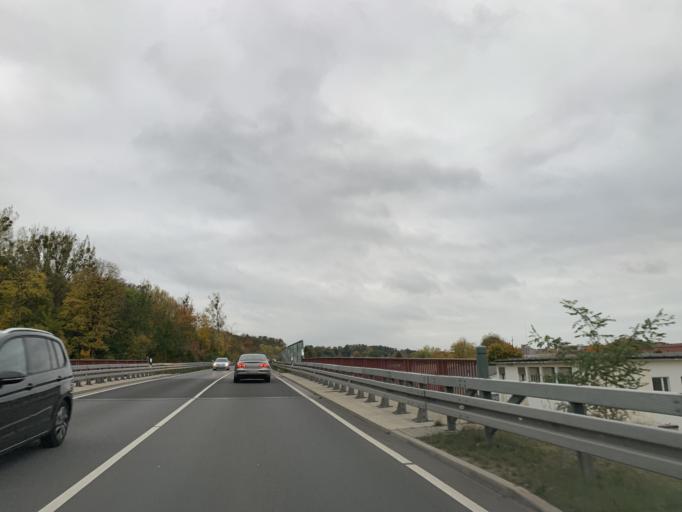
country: DE
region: Mecklenburg-Vorpommern
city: Neubrandenburg
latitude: 53.5503
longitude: 13.2756
